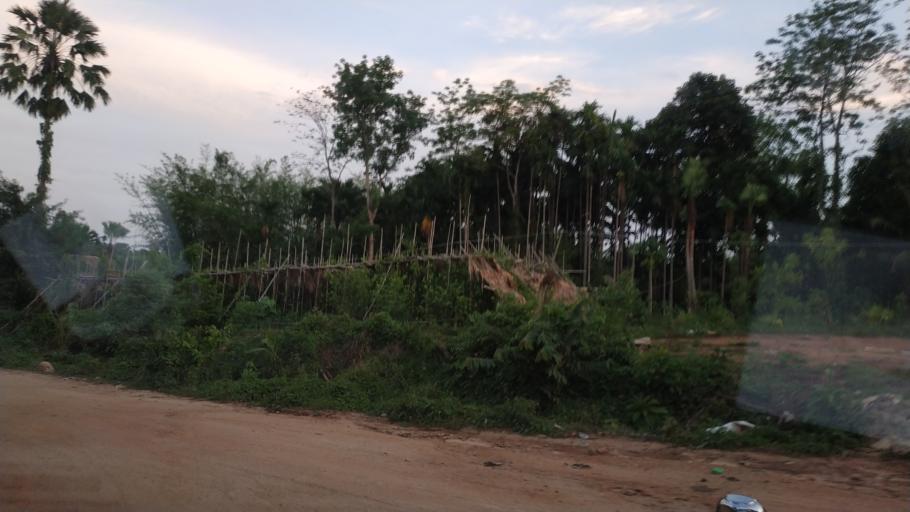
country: MM
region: Mon
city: Kyaikto
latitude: 17.4319
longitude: 97.0401
